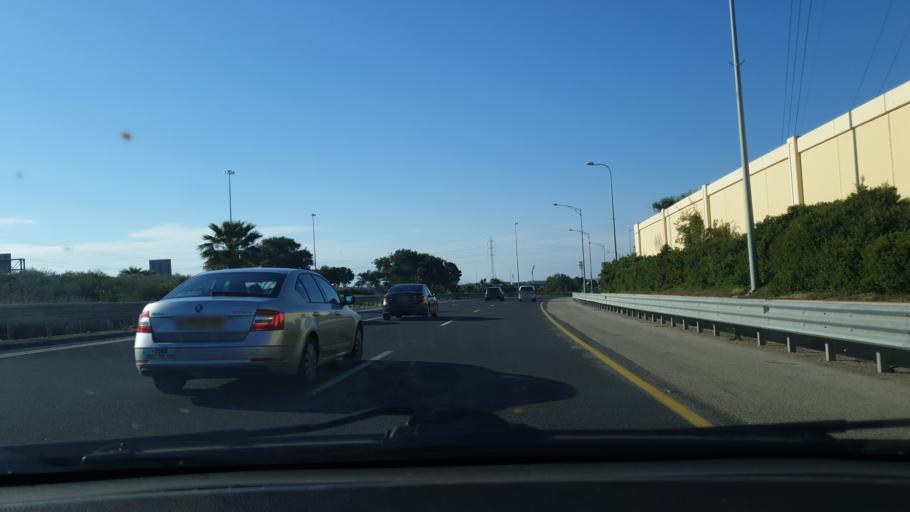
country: IL
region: Central District
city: Rishon LeZiyyon
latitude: 31.9680
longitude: 34.7598
